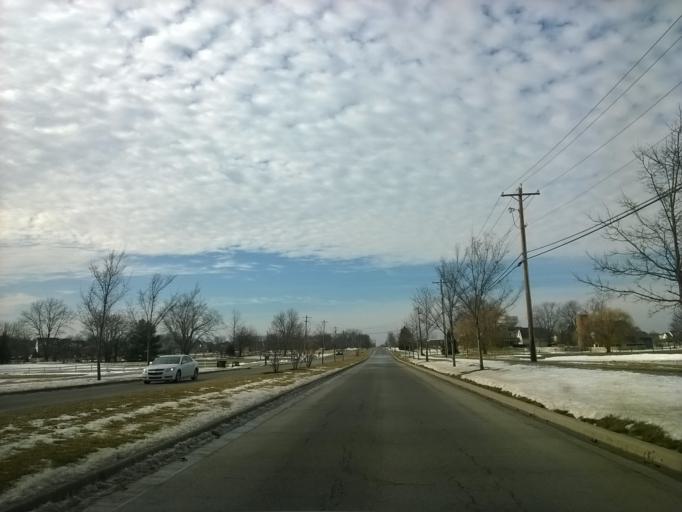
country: US
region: Indiana
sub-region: Boone County
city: Zionsville
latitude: 39.9774
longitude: -86.2104
